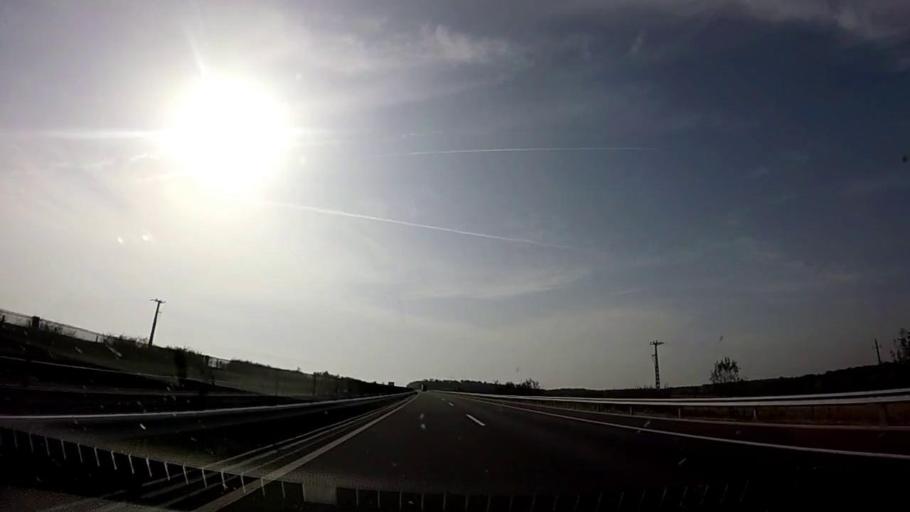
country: HU
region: Zala
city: Zalakomar
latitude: 46.5994
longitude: 17.2513
